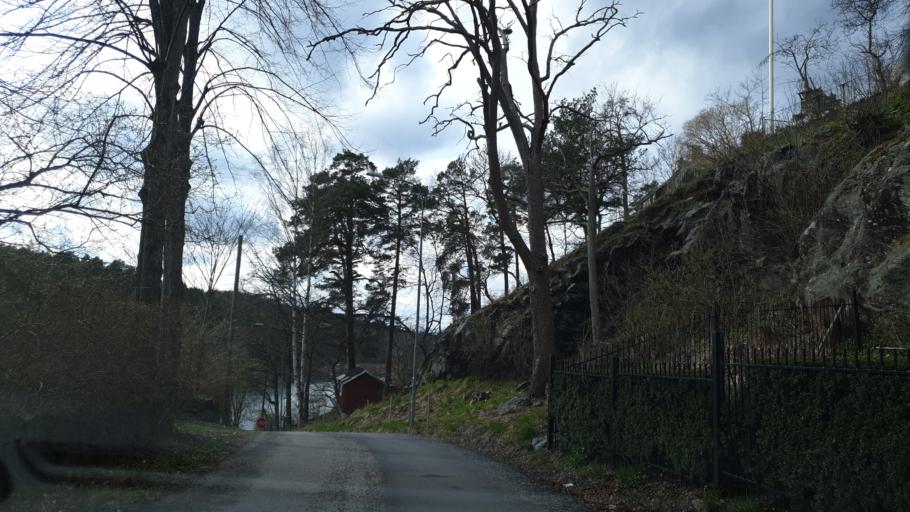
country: SE
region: Stockholm
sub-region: Nacka Kommun
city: Saltsjobaden
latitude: 59.2778
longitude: 18.3028
